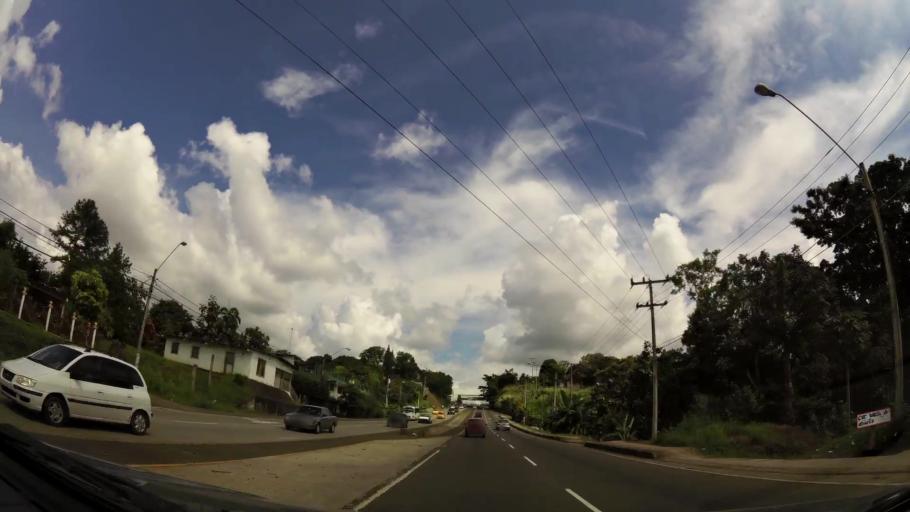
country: PA
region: Panama
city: Vista Alegre
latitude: 8.9372
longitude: -79.6844
